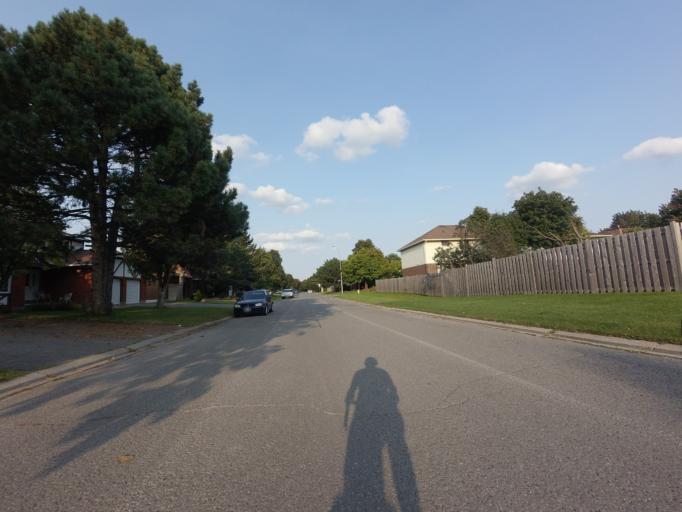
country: CA
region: Ontario
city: Bells Corners
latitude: 45.2939
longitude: -75.7440
